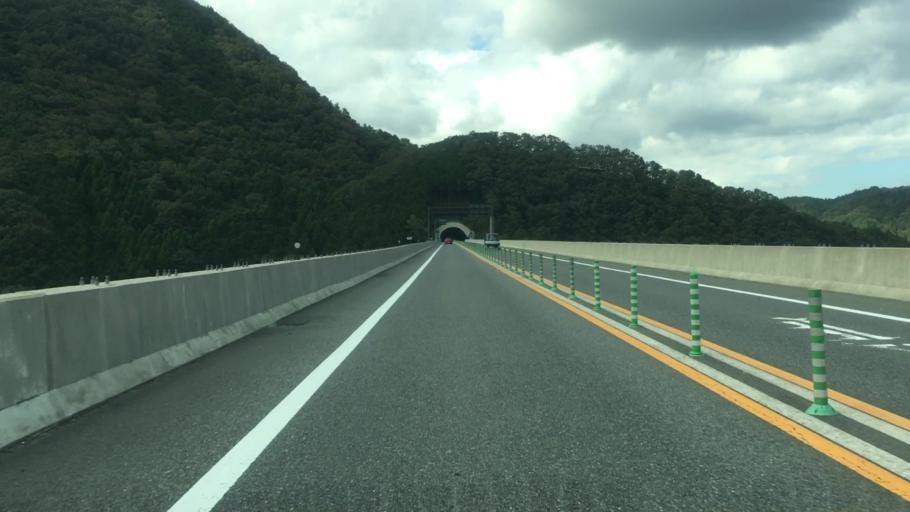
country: JP
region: Hyogo
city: Toyooka
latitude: 35.3187
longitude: 134.8441
